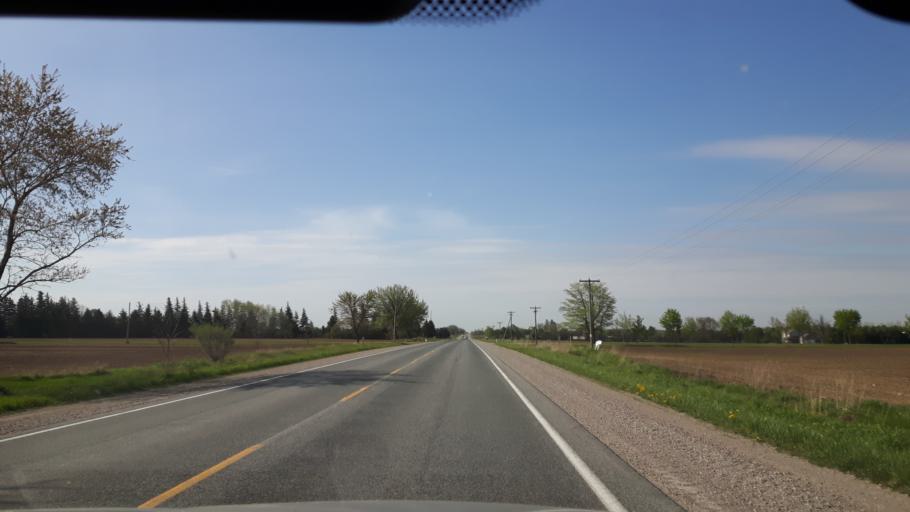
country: CA
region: Ontario
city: Bluewater
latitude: 43.5148
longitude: -81.5151
